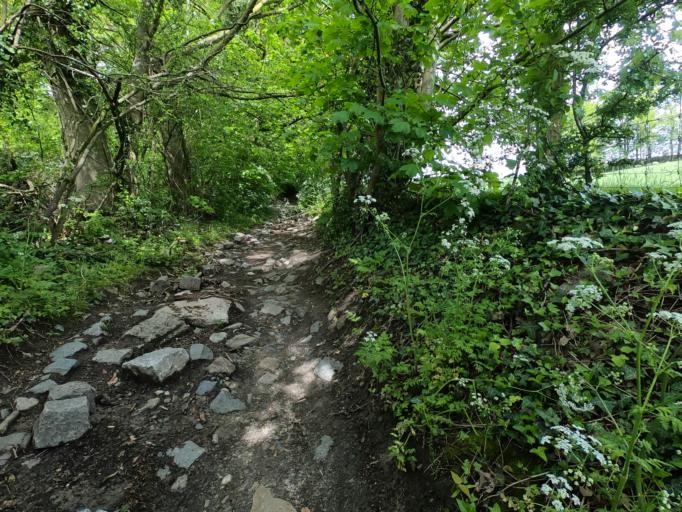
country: BE
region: Flanders
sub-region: Provincie Oost-Vlaanderen
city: Ronse
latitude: 50.7827
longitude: 3.5846
